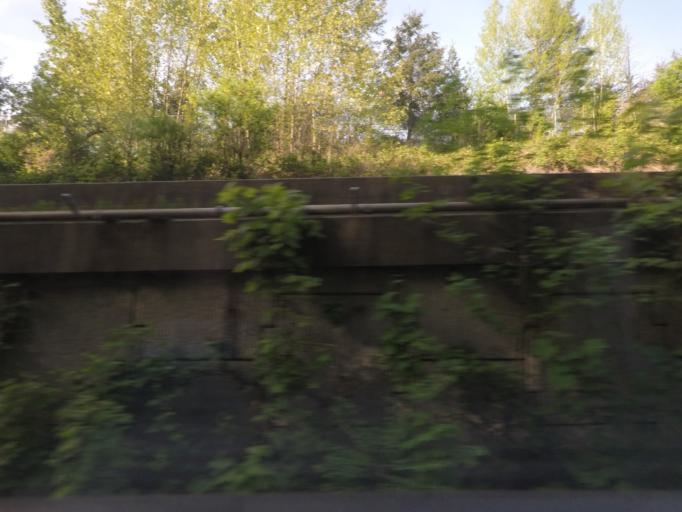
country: CA
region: British Columbia
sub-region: Fraser Valley Regional District
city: North Vancouver
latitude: 49.2589
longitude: -123.0584
